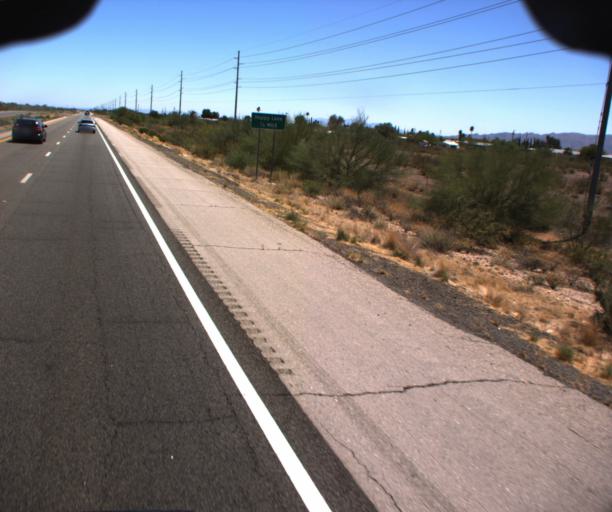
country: US
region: Arizona
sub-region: Maricopa County
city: Sun City West
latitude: 33.7914
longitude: -112.5462
